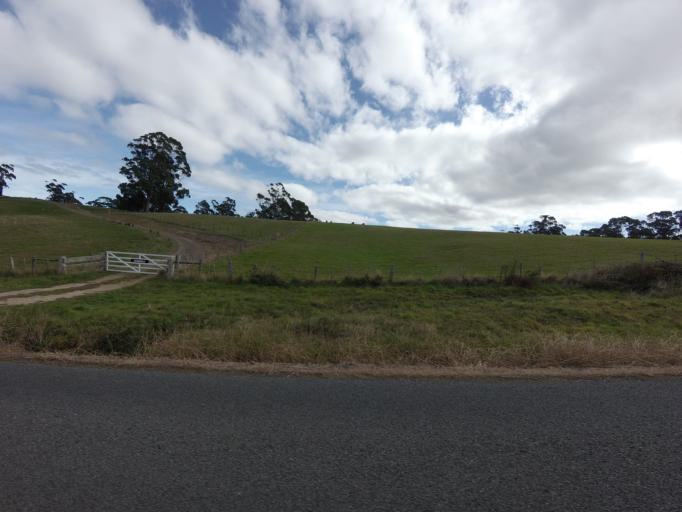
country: AU
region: Tasmania
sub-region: Clarence
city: Sandford
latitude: -43.0766
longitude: 147.7487
